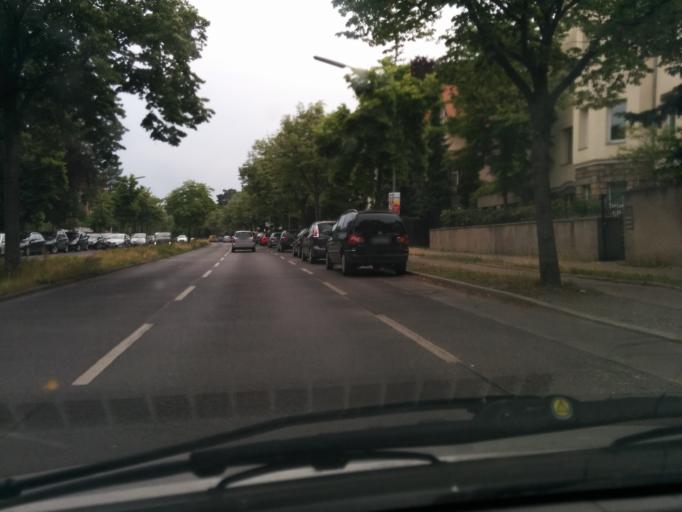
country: DE
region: Berlin
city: Zehlendorf Bezirk
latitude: 52.4365
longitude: 13.2309
